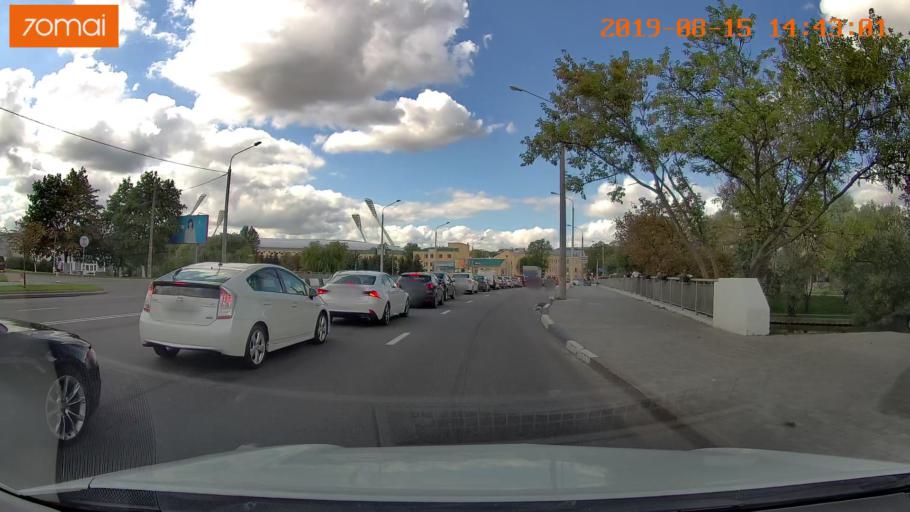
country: BY
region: Minsk
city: Minsk
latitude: 53.8947
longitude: 27.5677
